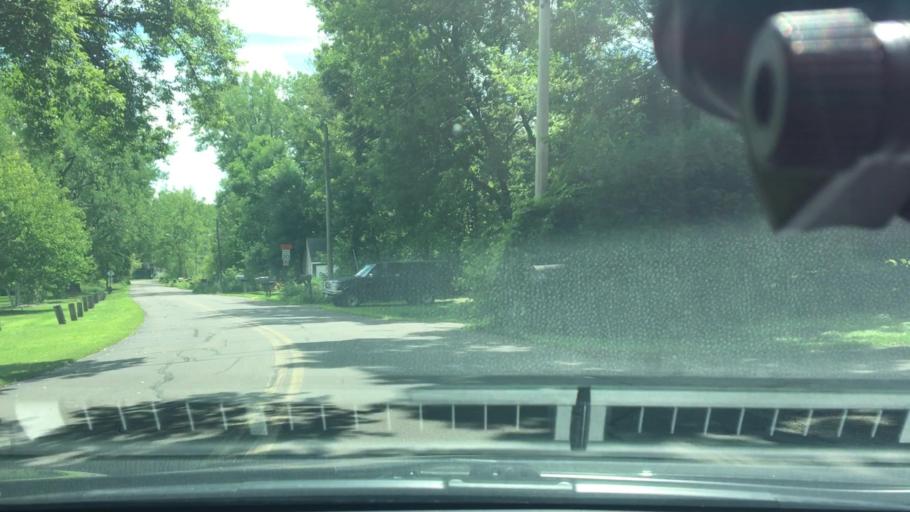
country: US
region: Minnesota
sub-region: Hennepin County
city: Plymouth
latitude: 45.0023
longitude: -93.4245
